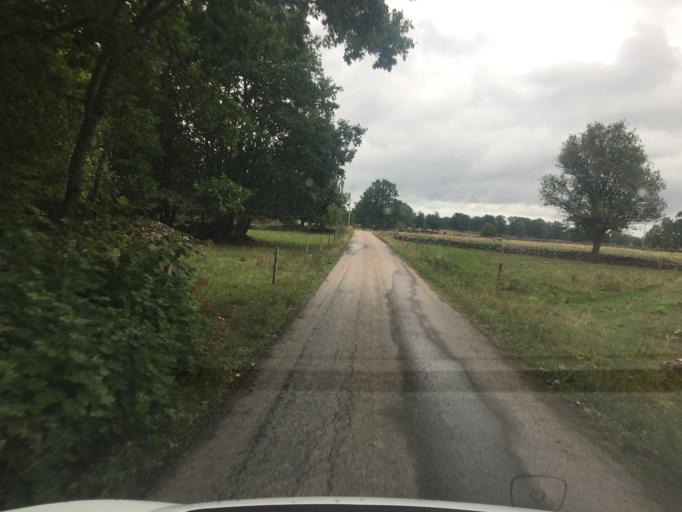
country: SE
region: Kronoberg
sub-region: Ljungby Kommun
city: Lagan
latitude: 56.9752
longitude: 14.0384
